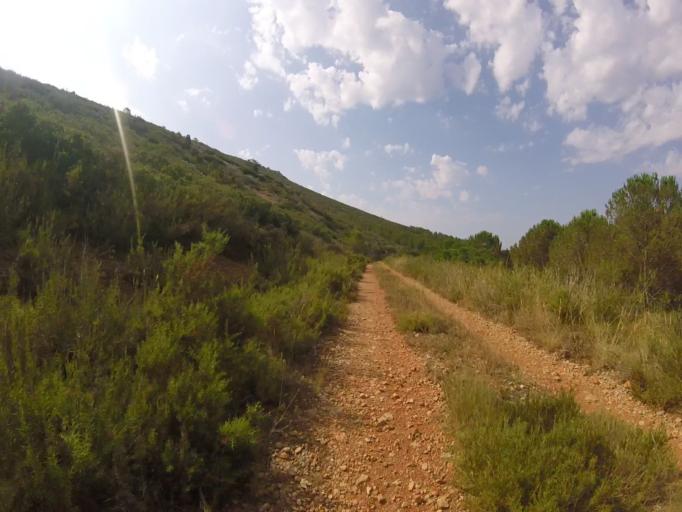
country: ES
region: Valencia
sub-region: Provincia de Castello
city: Alcala de Xivert
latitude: 40.3542
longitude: 0.2003
